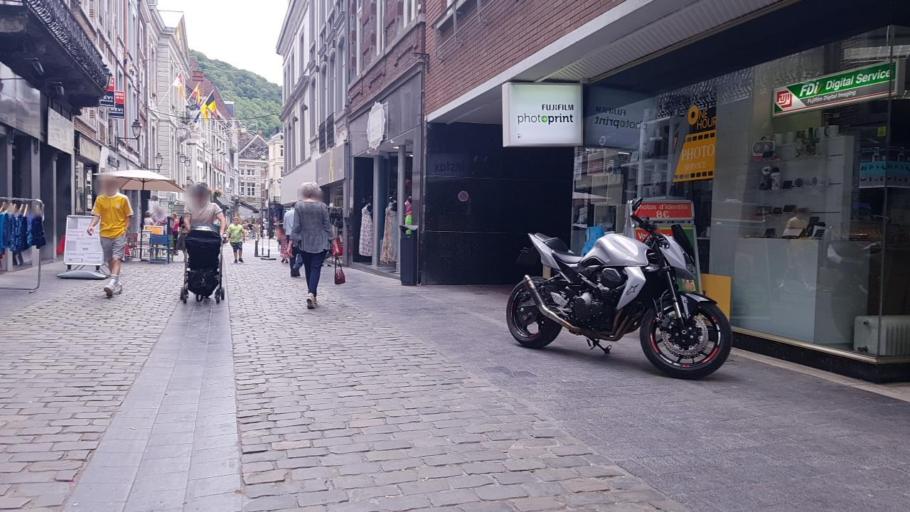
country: BE
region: Wallonia
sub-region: Province de Liege
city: Huy
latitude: 50.5189
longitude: 5.2406
